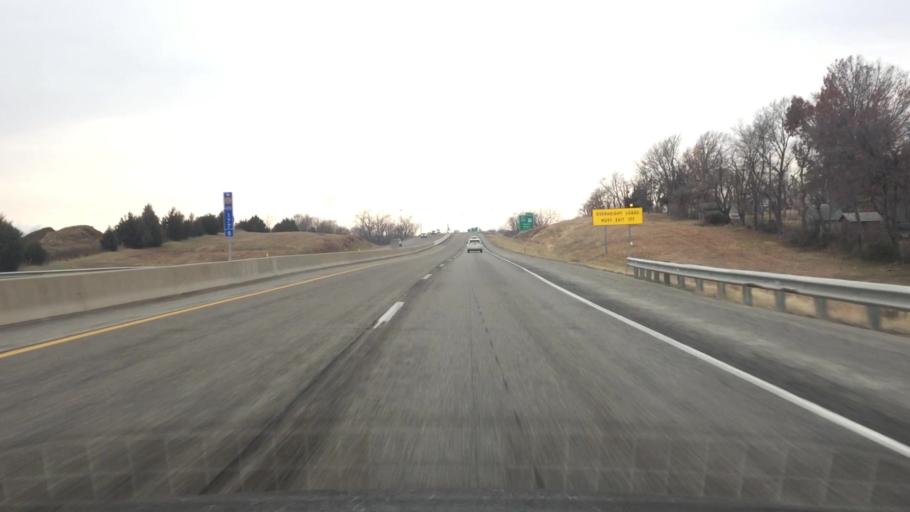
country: US
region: Kansas
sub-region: Shawnee County
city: Topeka
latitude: 38.9917
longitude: -95.6794
